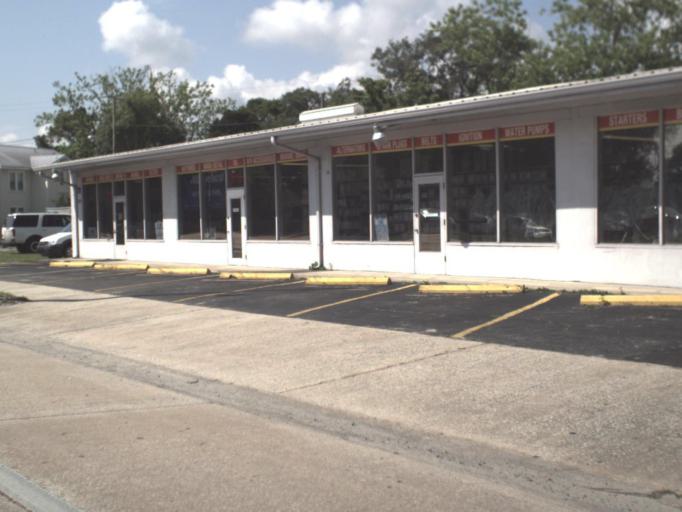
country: US
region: Florida
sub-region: Saint Johns County
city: Saint Augustine
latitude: 29.8885
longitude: -81.3243
